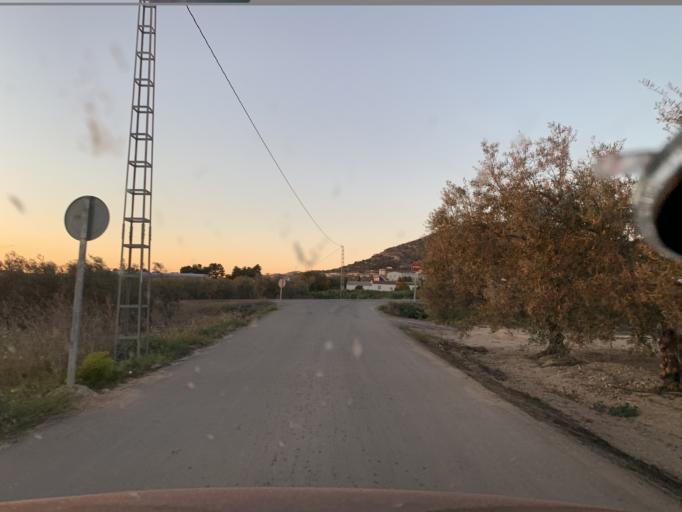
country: ES
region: Andalusia
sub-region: Provincia de Sevilla
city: Gilena
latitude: 37.2432
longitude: -4.9218
